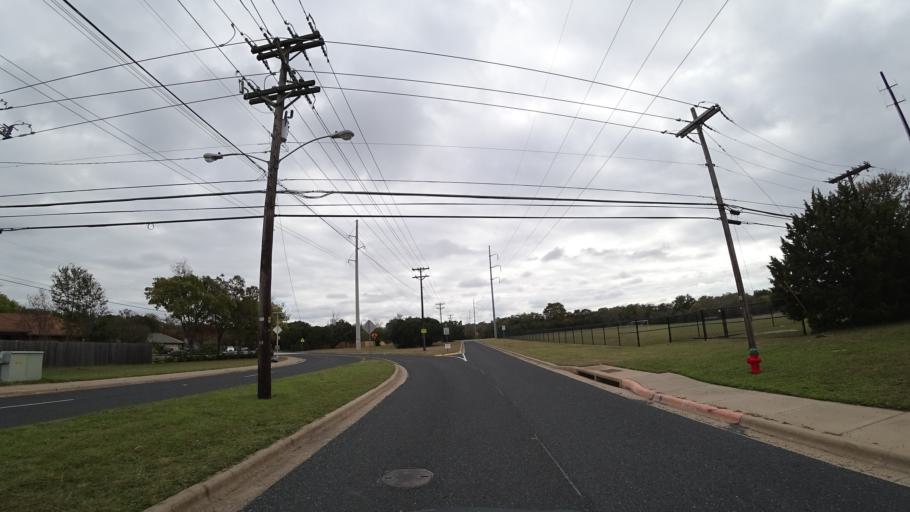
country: US
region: Texas
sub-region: Williamson County
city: Round Rock
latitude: 30.5042
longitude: -97.6998
